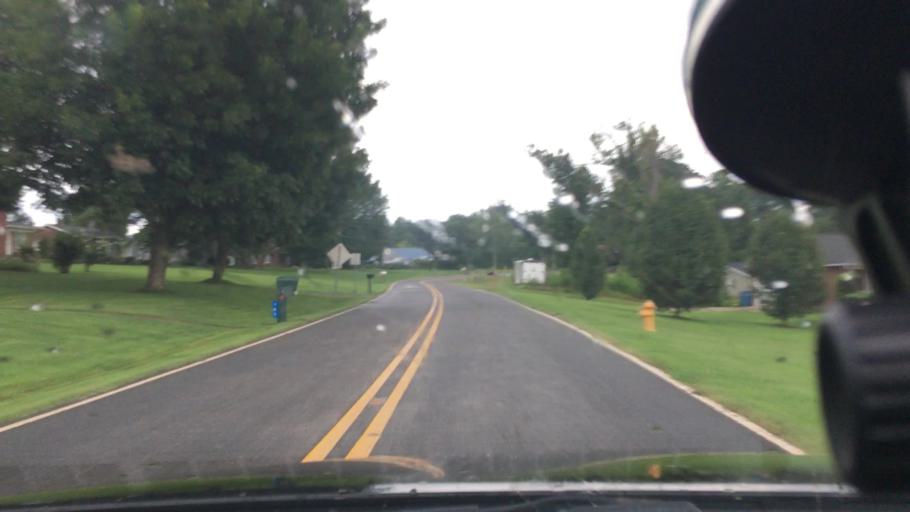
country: US
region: North Carolina
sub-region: Rutherford County
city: Rutherfordton
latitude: 35.3953
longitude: -81.9853
